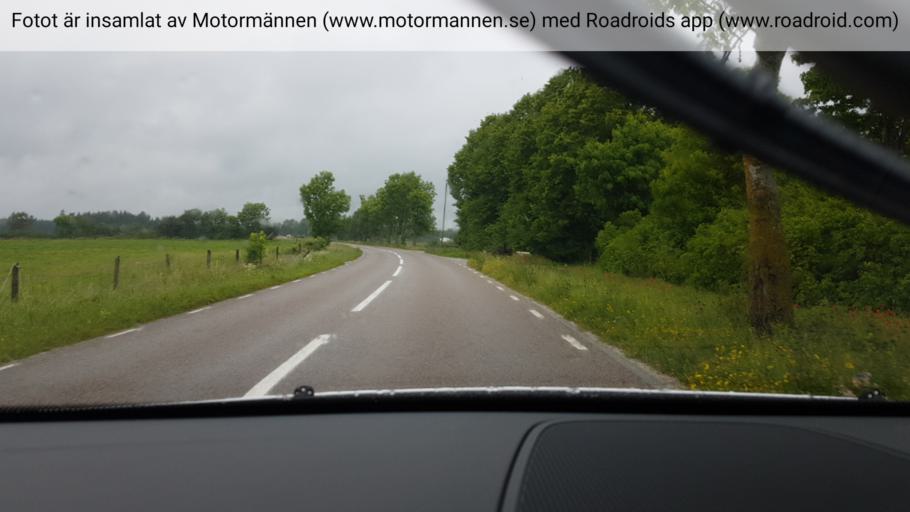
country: SE
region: Gotland
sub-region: Gotland
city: Slite
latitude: 57.6470
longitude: 18.7691
